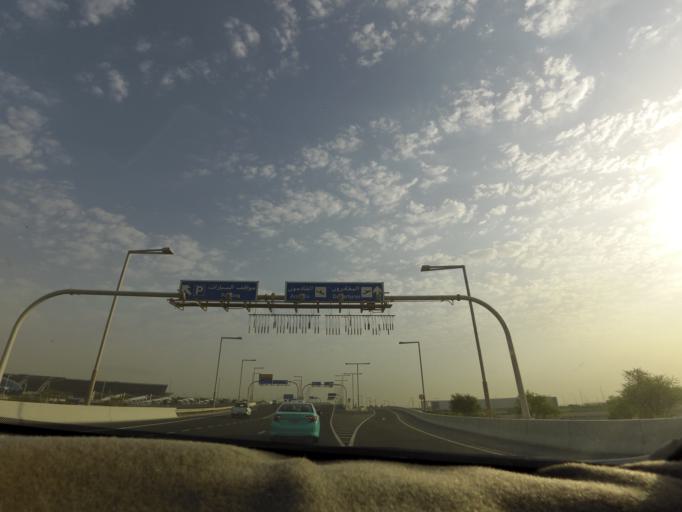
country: QA
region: Al Wakrah
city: Al Wakrah
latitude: 25.2562
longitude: 51.6170
